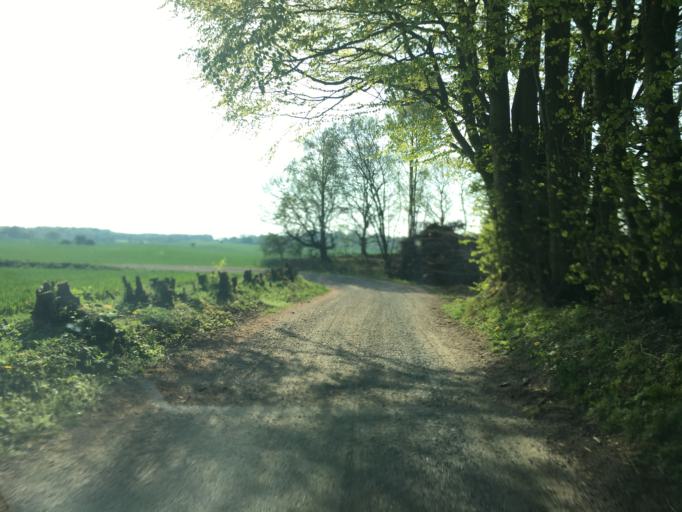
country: DK
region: South Denmark
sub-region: Aabenraa Kommune
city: Lojt Kirkeby
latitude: 55.1560
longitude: 9.3874
